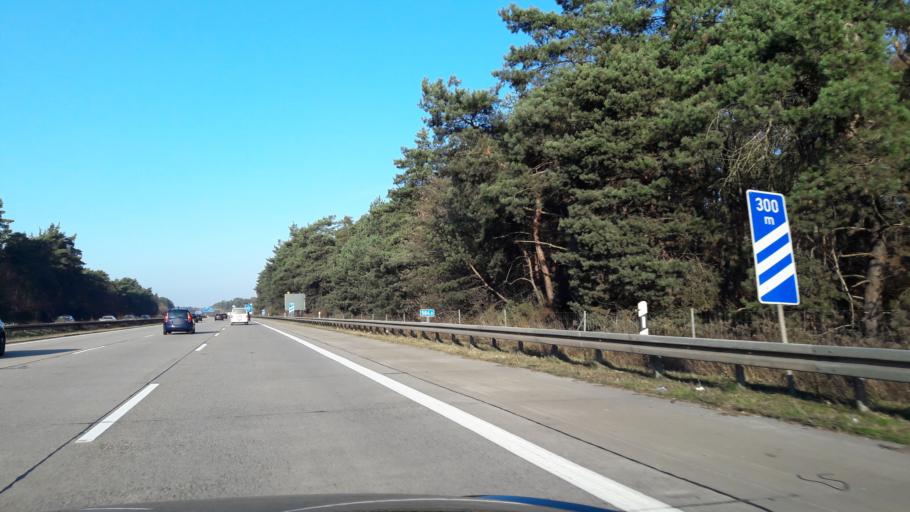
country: DE
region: Baden-Wuerttemberg
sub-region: Karlsruhe Region
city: Reilingen
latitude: 49.3102
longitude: 8.5829
